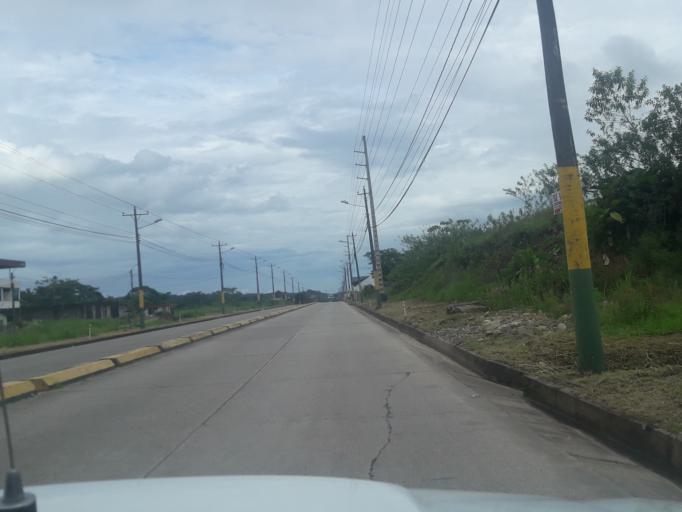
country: EC
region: Napo
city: Archidona
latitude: -0.9478
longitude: -77.8172
